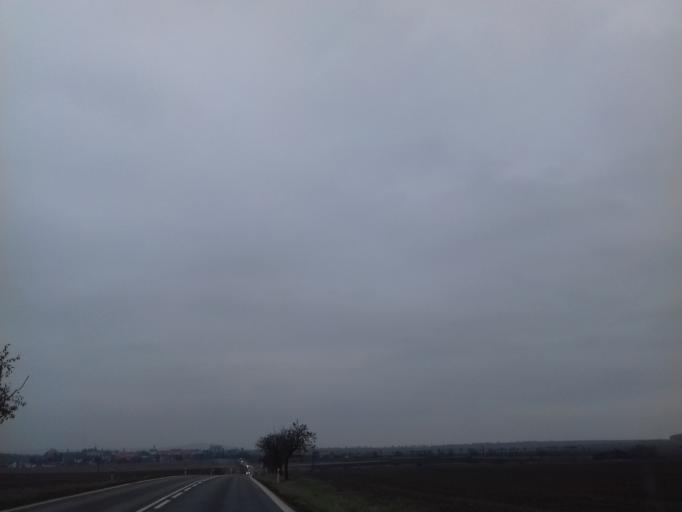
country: CZ
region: Plzensky
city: Zbuch
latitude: 49.6690
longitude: 13.2123
